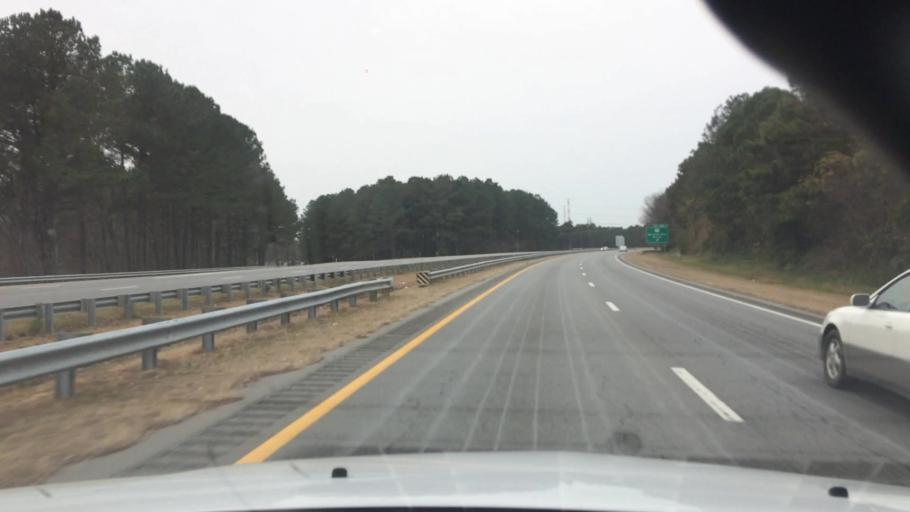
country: US
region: North Carolina
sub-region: Nash County
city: Rocky Mount
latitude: 35.9646
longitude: -77.8137
